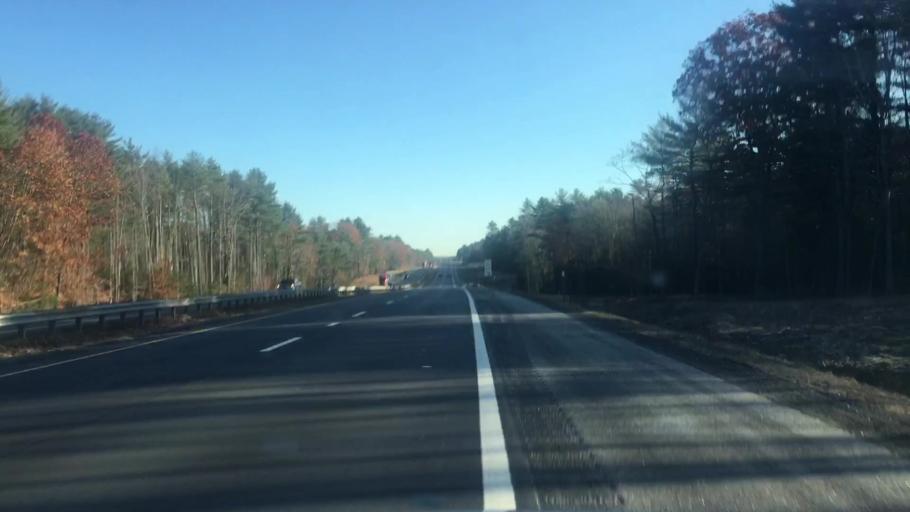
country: US
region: Maine
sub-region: Androscoggin County
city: Auburn
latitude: 44.0412
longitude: -70.2562
